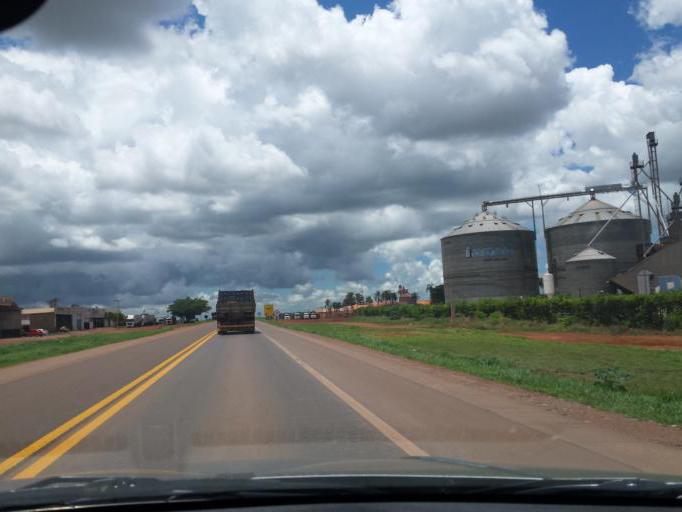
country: BR
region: Goias
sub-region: Cristalina
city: Cristalina
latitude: -16.7759
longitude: -47.6243
